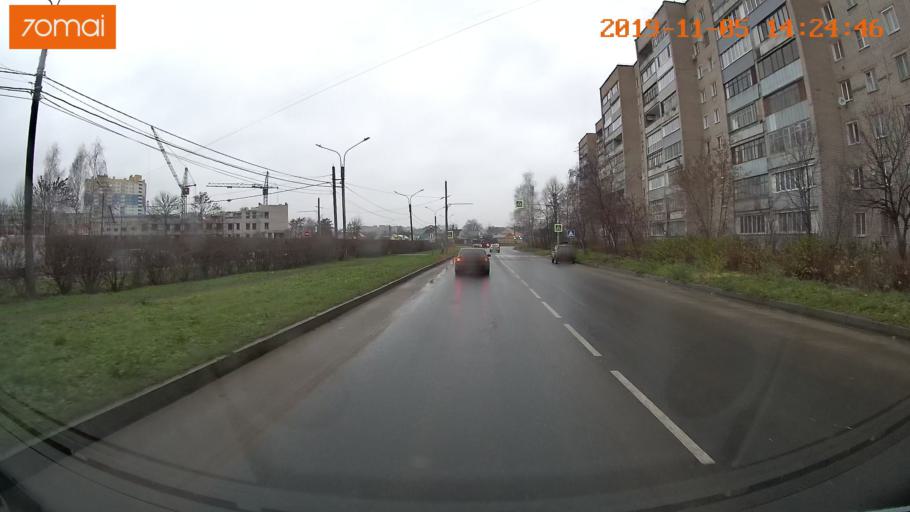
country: RU
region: Ivanovo
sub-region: Gorod Ivanovo
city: Ivanovo
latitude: 56.9699
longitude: 40.9953
